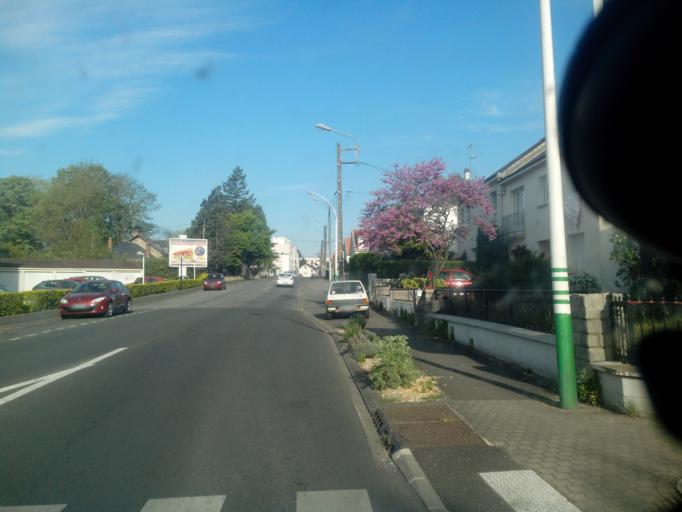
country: FR
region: Pays de la Loire
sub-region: Departement de la Loire-Atlantique
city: Orvault
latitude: 47.2397
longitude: -1.6020
